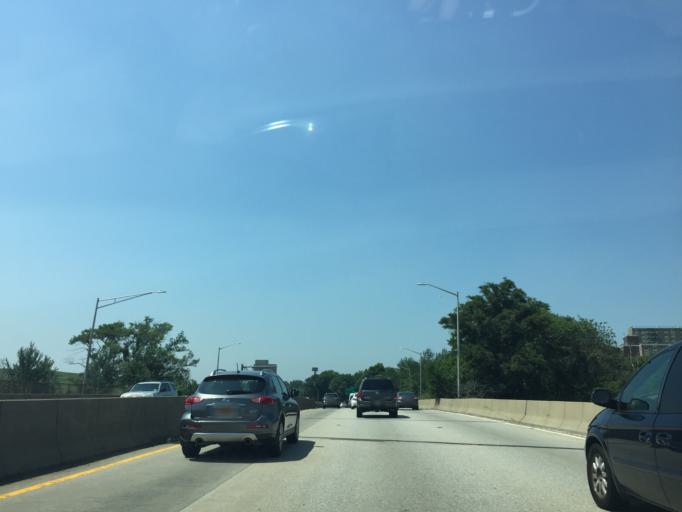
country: US
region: New York
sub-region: Kings County
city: East New York
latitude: 40.6468
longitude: -73.8736
